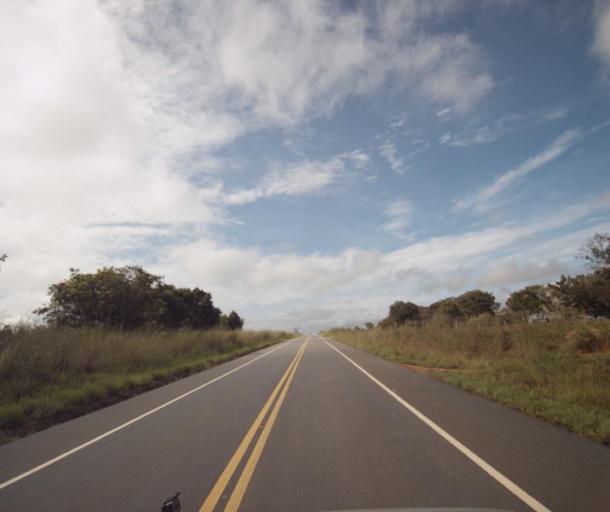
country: BR
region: Goias
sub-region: Barro Alto
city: Barro Alto
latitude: -15.2834
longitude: -48.6805
